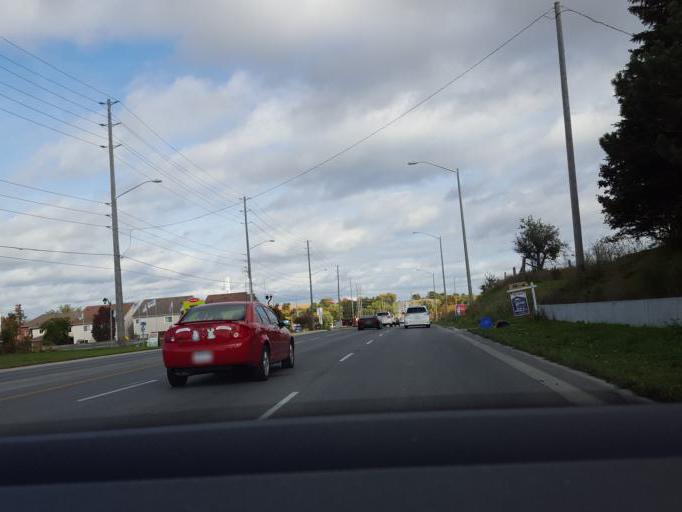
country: CA
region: Ontario
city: Oshawa
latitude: 43.9430
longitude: -78.8340
